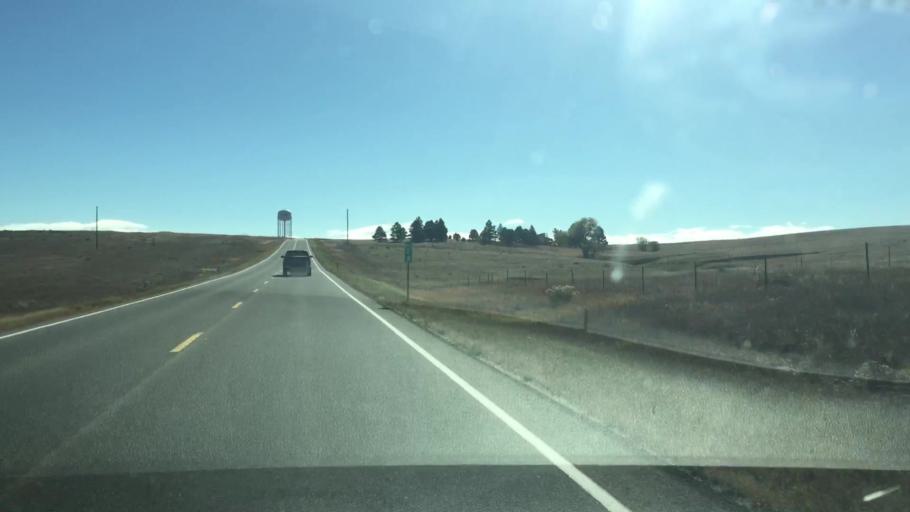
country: US
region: Colorado
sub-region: Elbert County
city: Kiowa
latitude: 39.3434
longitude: -104.4484
